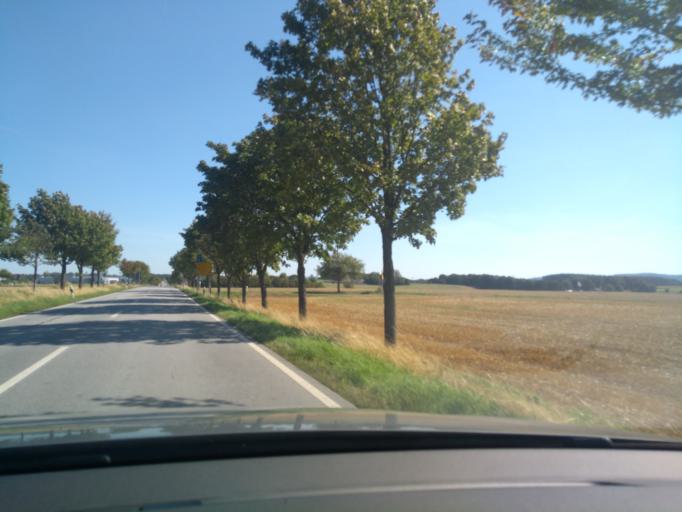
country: DE
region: Saxony
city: Goda
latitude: 51.1955
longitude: 14.3297
